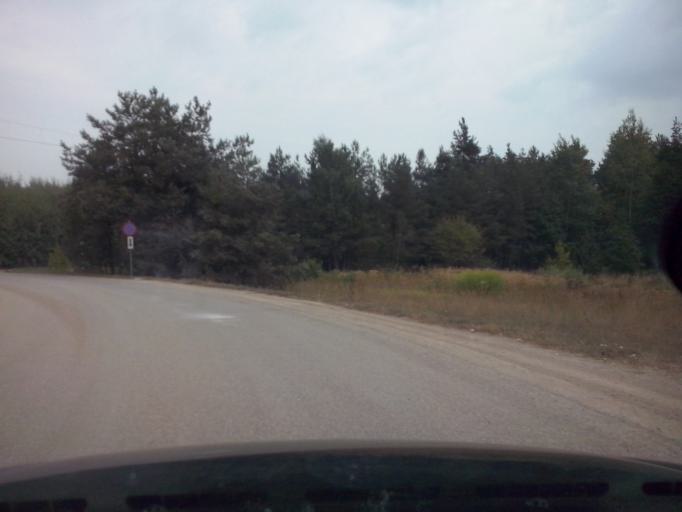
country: PL
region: Swietokrzyskie
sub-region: Kielce
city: Osiedle-Nowiny
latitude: 50.7842
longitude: 20.5367
